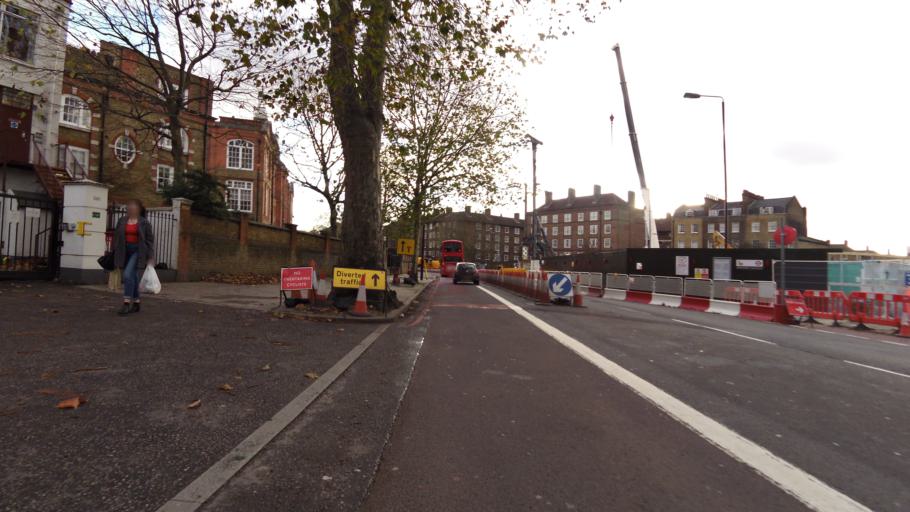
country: GB
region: England
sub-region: Greater London
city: Kennington
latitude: 51.4863
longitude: -0.1113
